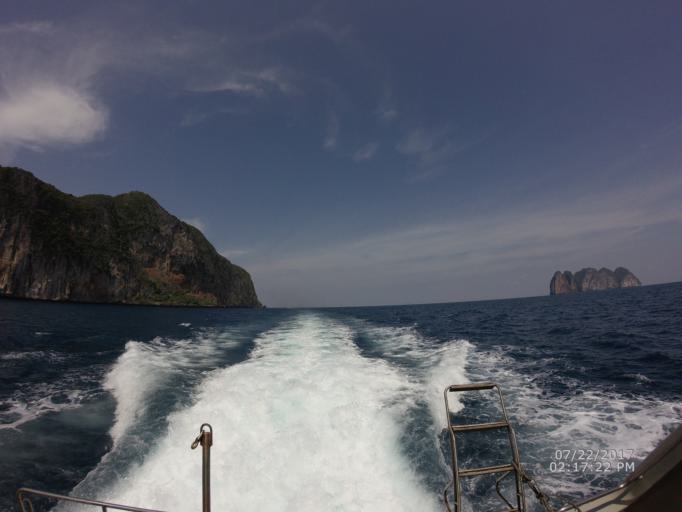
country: TH
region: Phangnga
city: Ban Phru Nai
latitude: 7.7208
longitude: 98.7576
